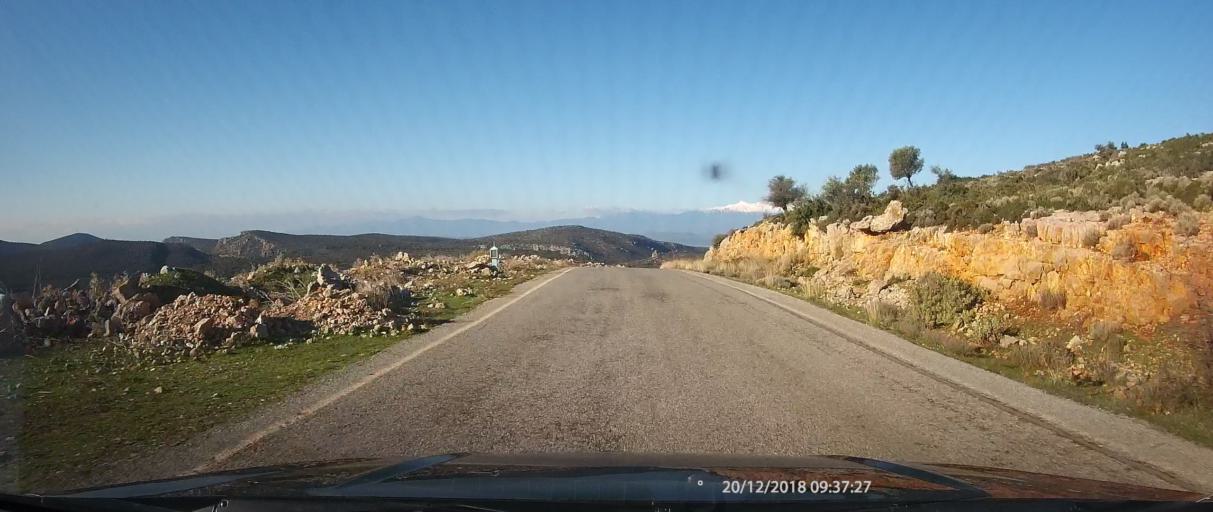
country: GR
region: Peloponnese
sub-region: Nomos Lakonias
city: Kato Glikovrisi
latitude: 36.9380
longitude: 22.8083
